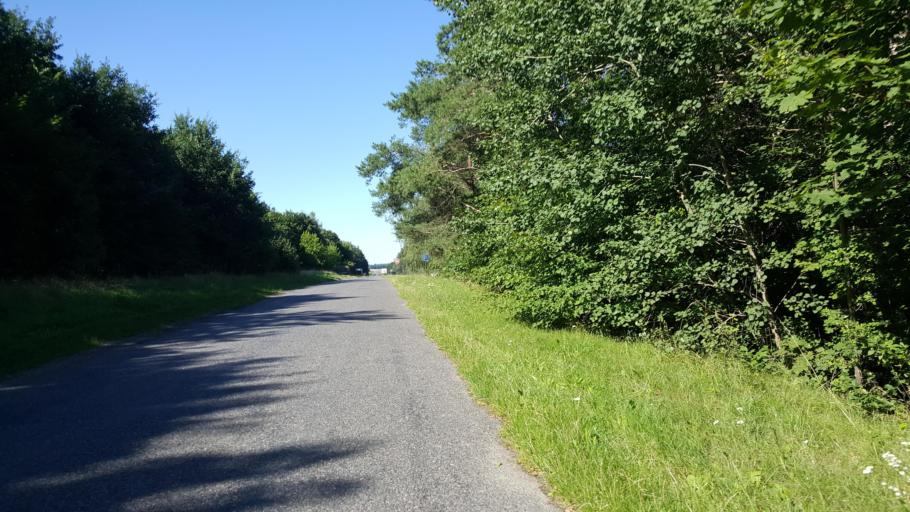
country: BY
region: Brest
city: Charnawchytsy
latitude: 52.2381
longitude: 23.7455
